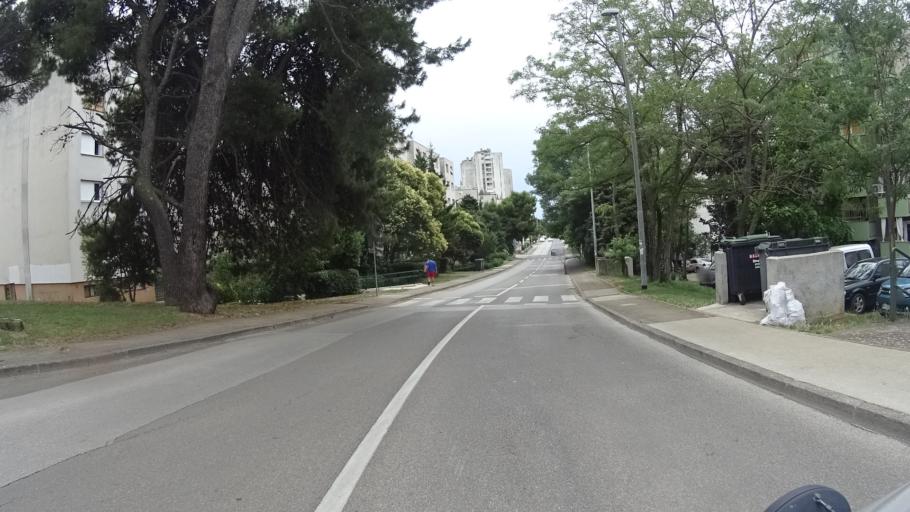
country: HR
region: Istarska
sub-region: Grad Pula
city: Pula
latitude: 44.8565
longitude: 13.8439
